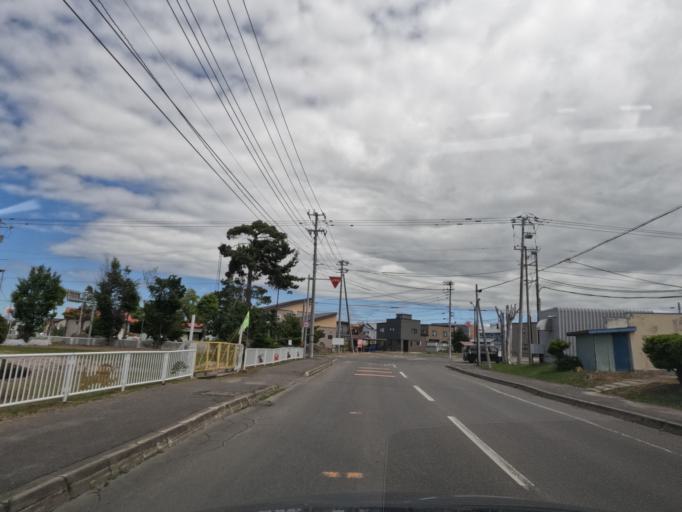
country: JP
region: Hokkaido
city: Shimo-furano
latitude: 43.4588
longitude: 142.4657
